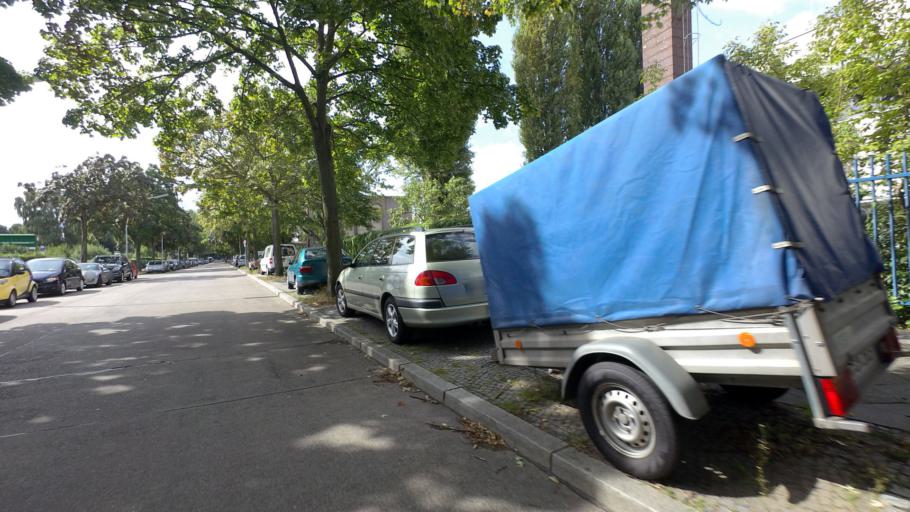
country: DE
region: Berlin
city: Tegel
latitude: 52.5734
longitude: 13.3038
